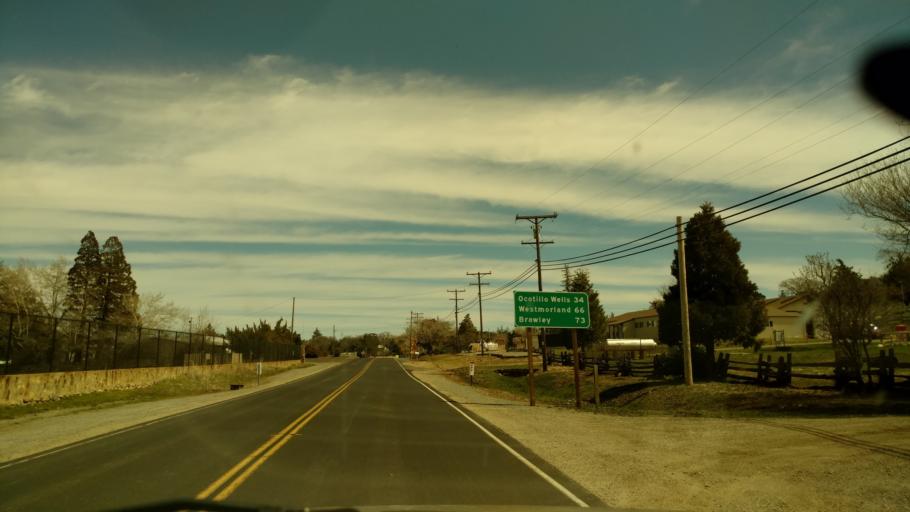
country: US
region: California
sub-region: San Diego County
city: Julian
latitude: 33.0765
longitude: -116.5940
